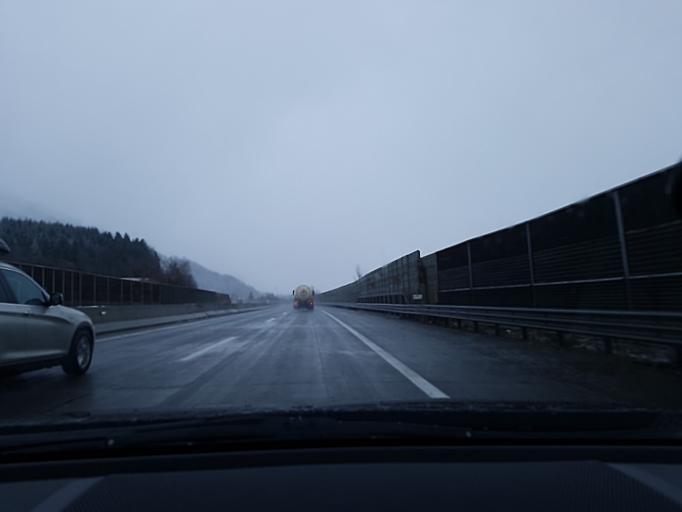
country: AT
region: Salzburg
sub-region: Politischer Bezirk Hallein
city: Golling an der Salzach
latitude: 47.6048
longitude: 13.1485
